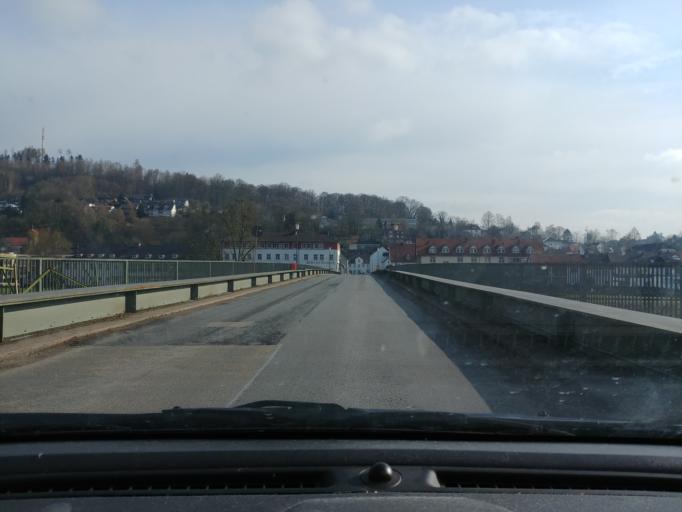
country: DE
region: Lower Saxony
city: Bad Karlshafen
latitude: 51.6452
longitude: 9.4509
